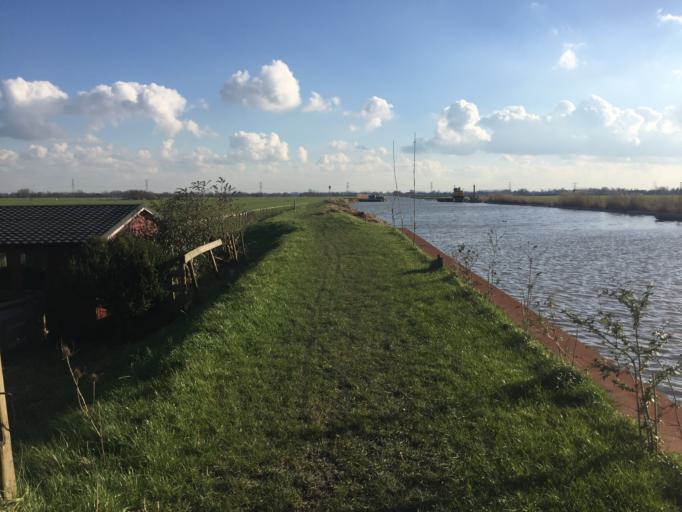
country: NL
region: South Holland
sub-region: Gemeente Vlist
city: Haastrecht
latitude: 52.0422
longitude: 4.8023
